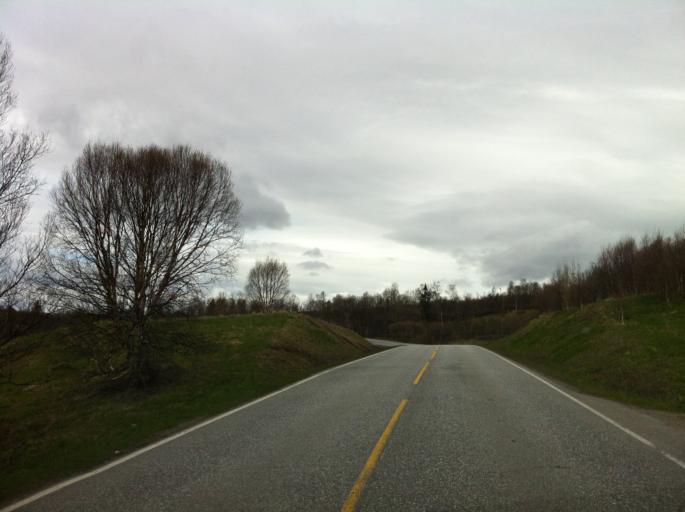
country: NO
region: Sor-Trondelag
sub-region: Roros
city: Roros
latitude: 62.5995
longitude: 11.5088
